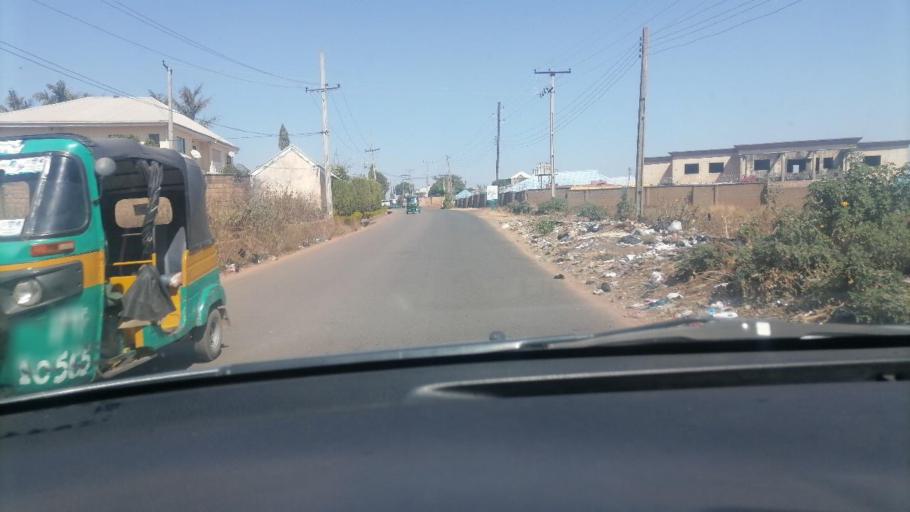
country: NG
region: Plateau
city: Jos
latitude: 9.8687
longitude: 8.9071
